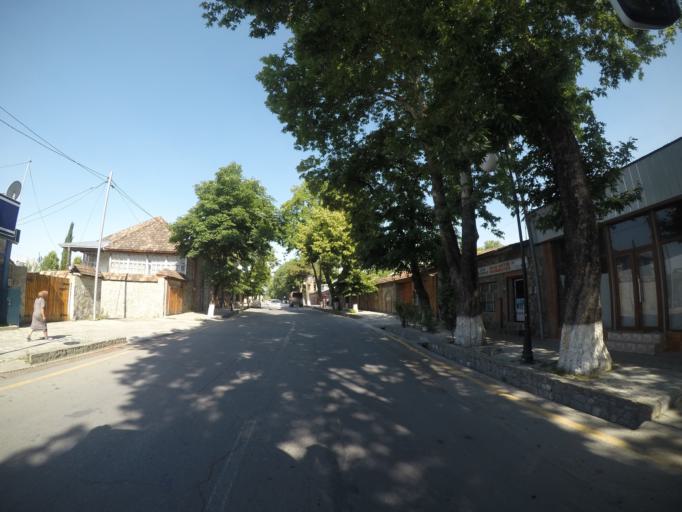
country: AZ
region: Shaki City
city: Sheki
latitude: 41.2057
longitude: 47.1755
